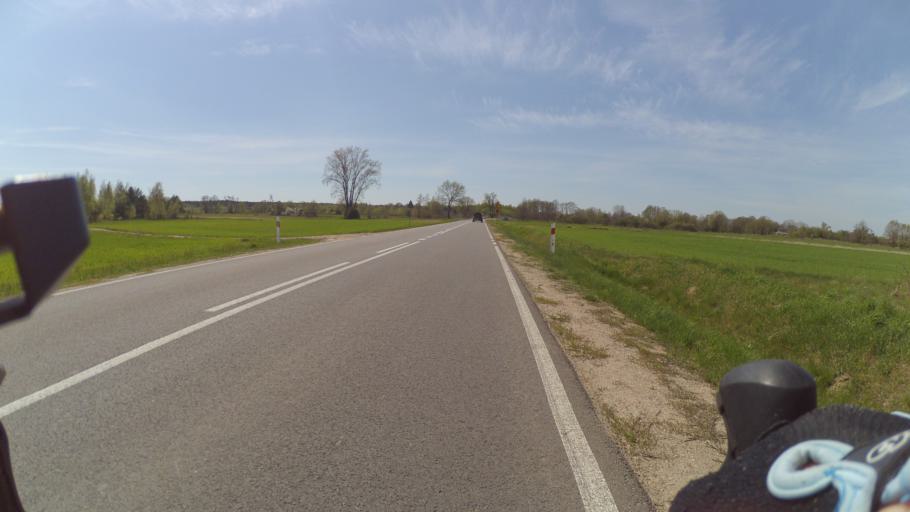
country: PL
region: Masovian Voivodeship
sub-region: Powiat plonski
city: Czerwinsk Nad Wisla
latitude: 52.3755
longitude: 20.3116
